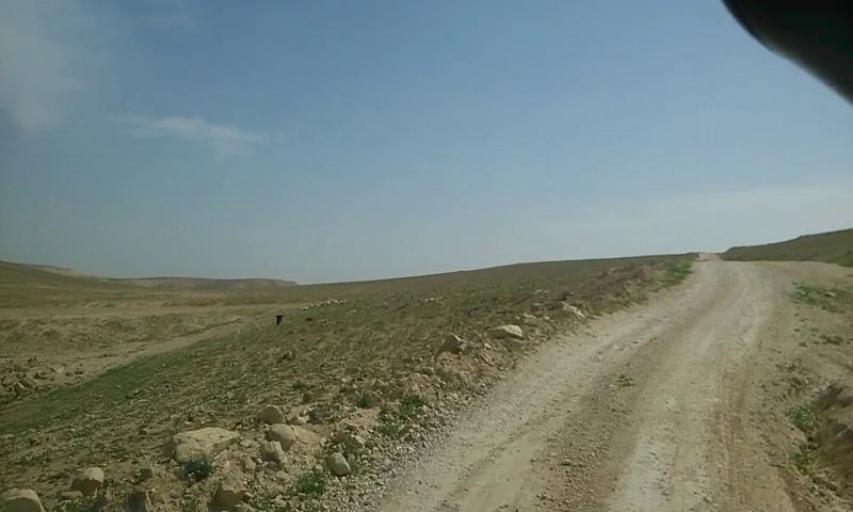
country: PS
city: `Arab ar Rashaydah
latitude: 31.5232
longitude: 35.2962
